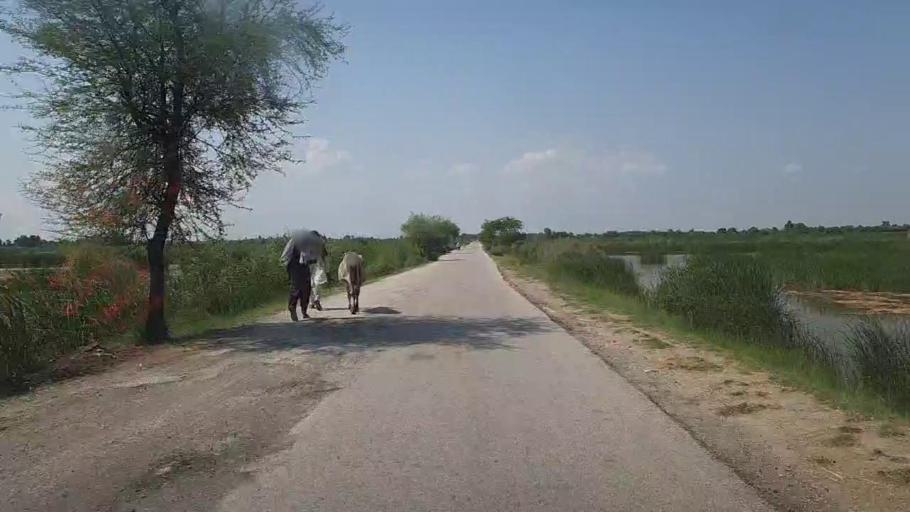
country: PK
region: Sindh
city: Khairpur
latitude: 28.0686
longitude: 69.6428
